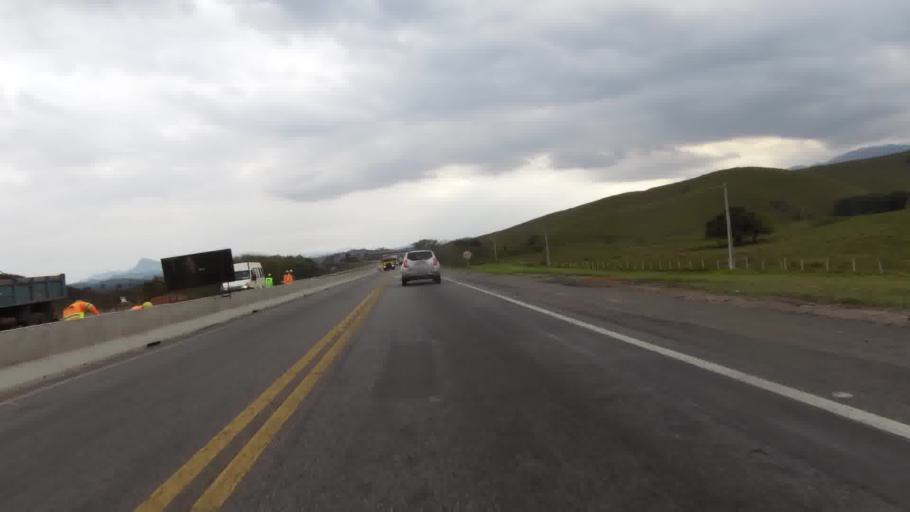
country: BR
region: Rio de Janeiro
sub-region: Rio Bonito
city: Rio Bonito
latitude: -22.6834
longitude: -42.5358
